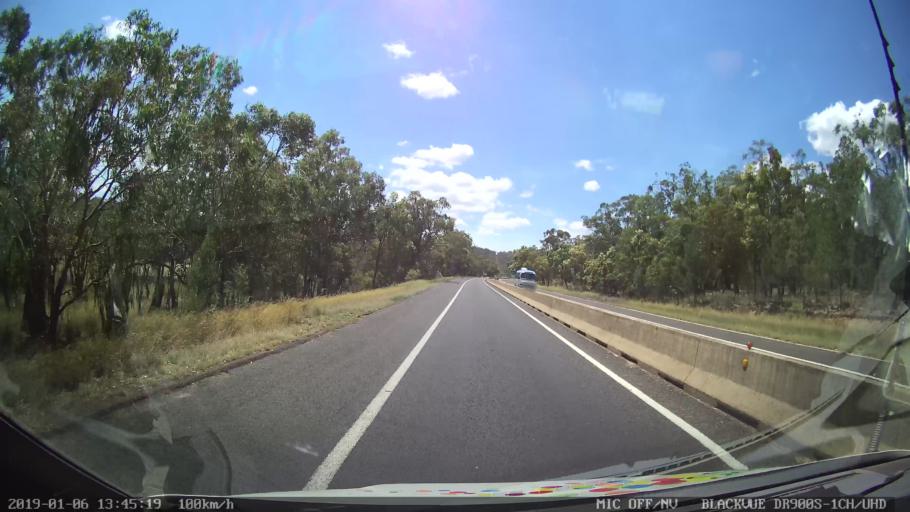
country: AU
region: New South Wales
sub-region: Tamworth Municipality
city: Kootingal
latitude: -30.9933
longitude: 151.0956
